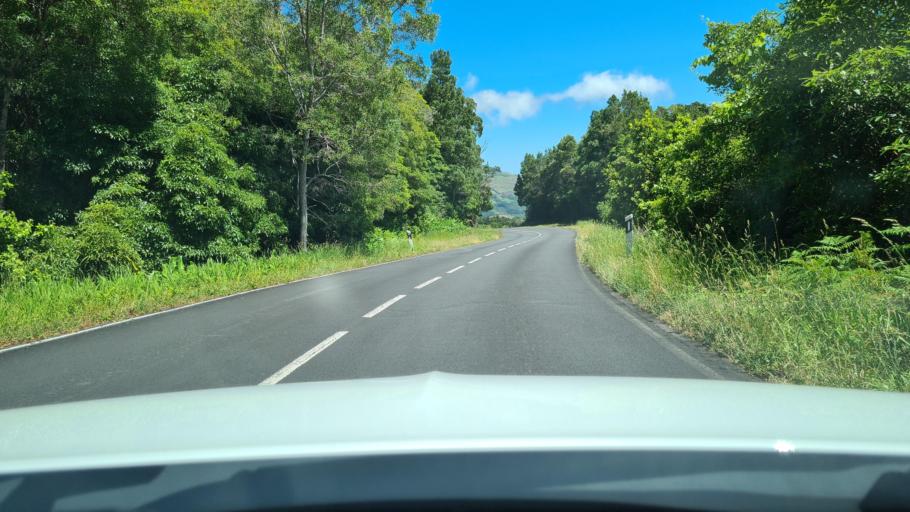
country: PT
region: Azores
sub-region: Sao Roque do Pico
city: Sao Roque do Pico
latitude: 38.4257
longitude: -28.2861
